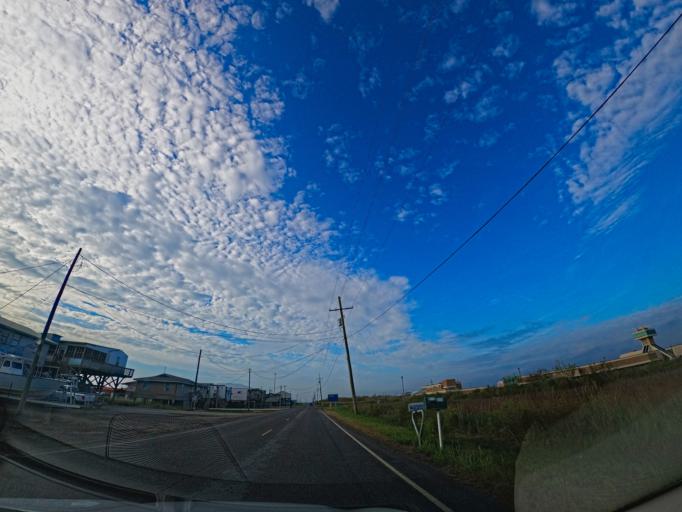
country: US
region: Louisiana
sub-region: Terrebonne Parish
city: Dulac
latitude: 29.2548
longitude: -90.6597
